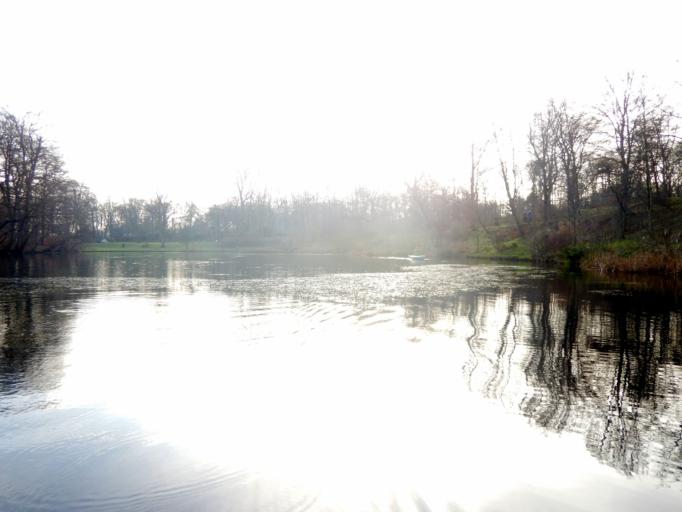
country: NL
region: North Holland
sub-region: Gemeente Bloemendaal
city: Bloemendaal
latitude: 52.3879
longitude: 4.6003
